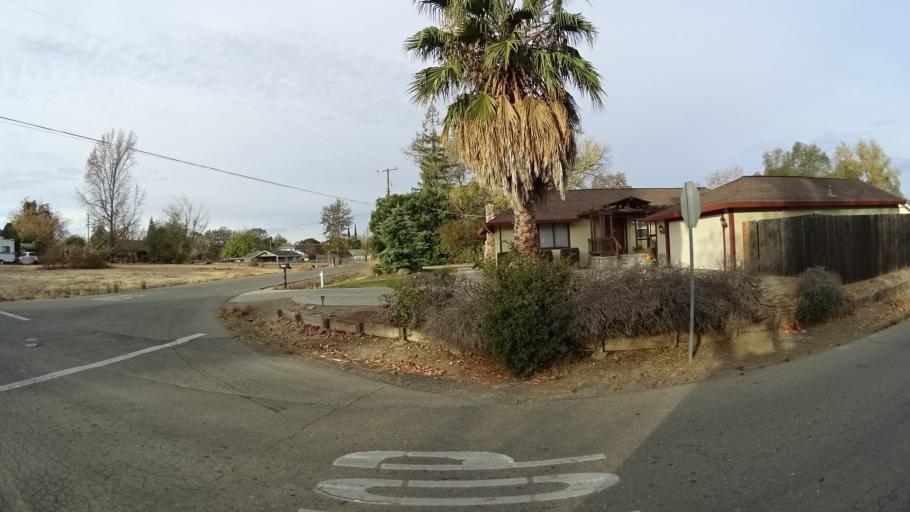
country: US
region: California
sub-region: Sacramento County
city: Citrus Heights
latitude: 38.7140
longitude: -121.2766
